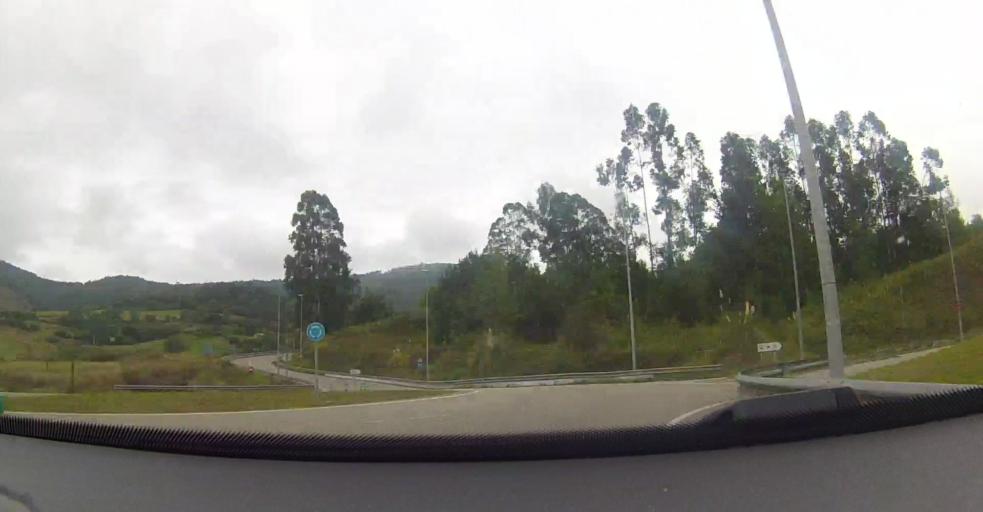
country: ES
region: Asturias
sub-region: Province of Asturias
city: Villaviciosa
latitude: 43.4890
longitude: -5.4458
